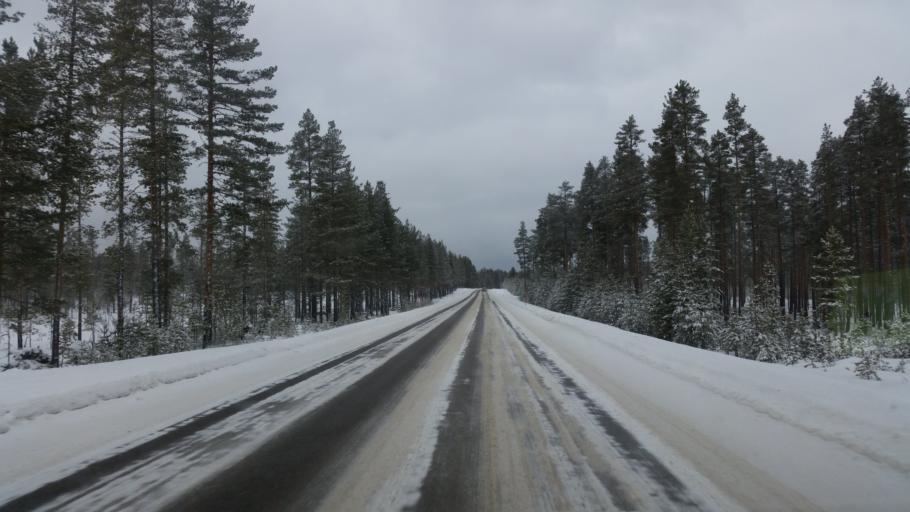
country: SE
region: Vaesternorrland
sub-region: Ange Kommun
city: Ange
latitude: 62.0629
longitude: 15.1122
